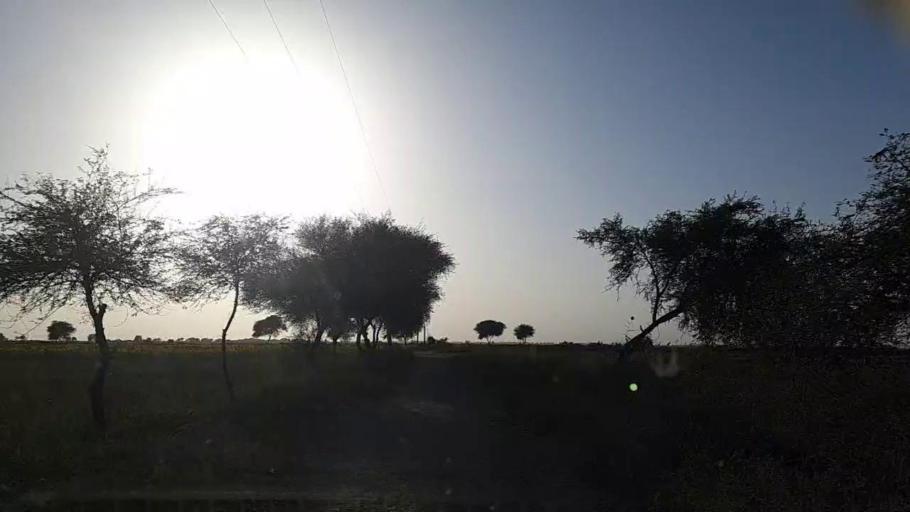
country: PK
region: Sindh
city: Jati
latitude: 24.4223
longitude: 68.2862
